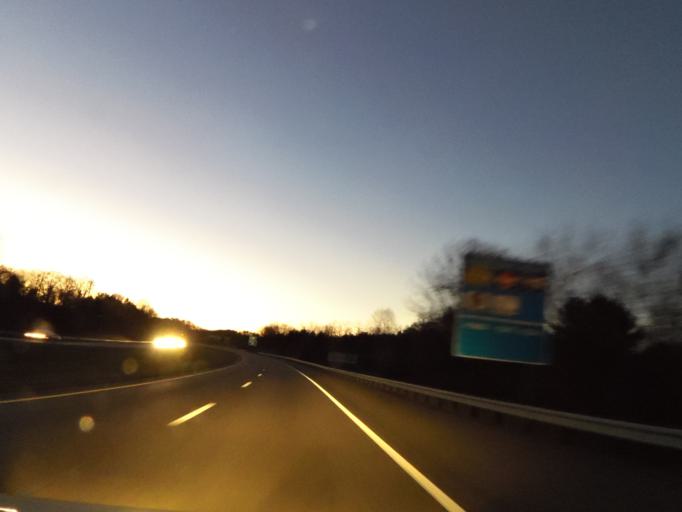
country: US
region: Tennessee
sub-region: Cocke County
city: Newport
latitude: 35.9686
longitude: -83.2270
